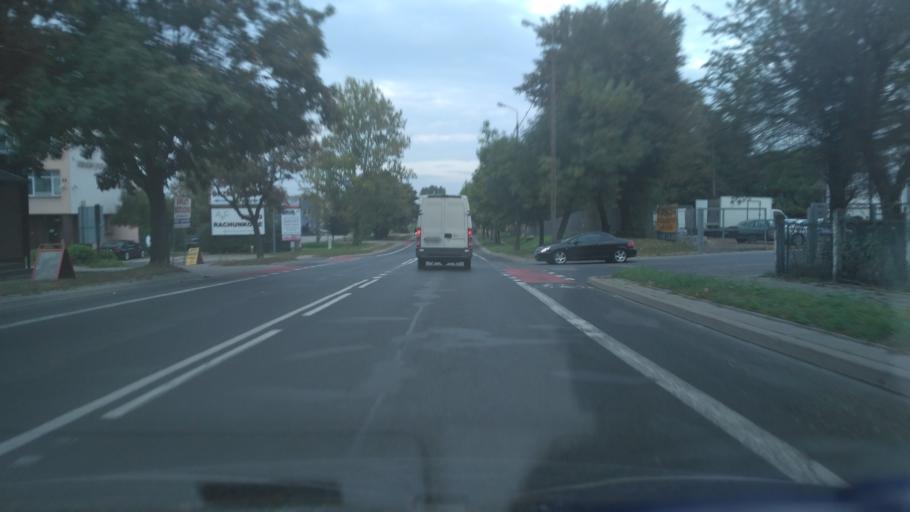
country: PL
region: Lublin Voivodeship
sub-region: Powiat lubelski
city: Jakubowice Murowane
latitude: 51.2555
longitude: 22.6063
